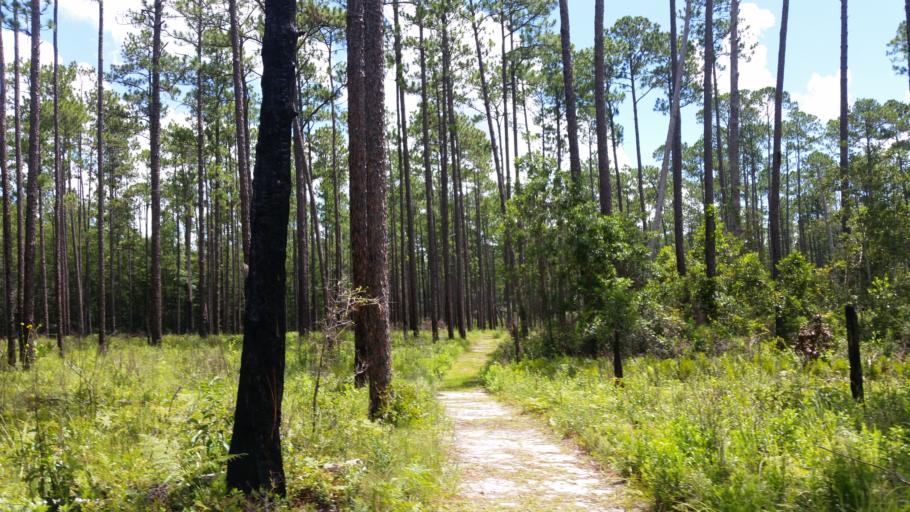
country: US
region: Florida
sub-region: Santa Rosa County
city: East Milton
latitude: 30.7046
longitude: -86.8756
